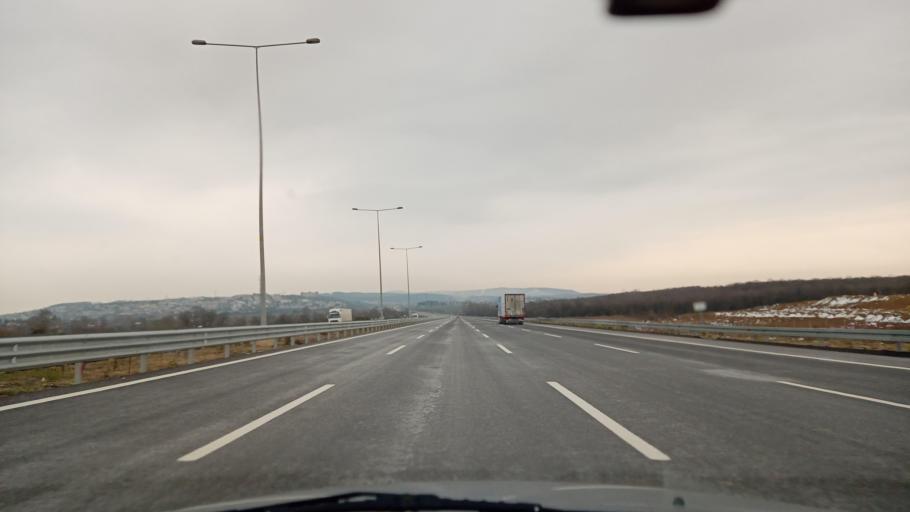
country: TR
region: Sakarya
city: Kazimpasa
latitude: 40.8435
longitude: 30.2973
